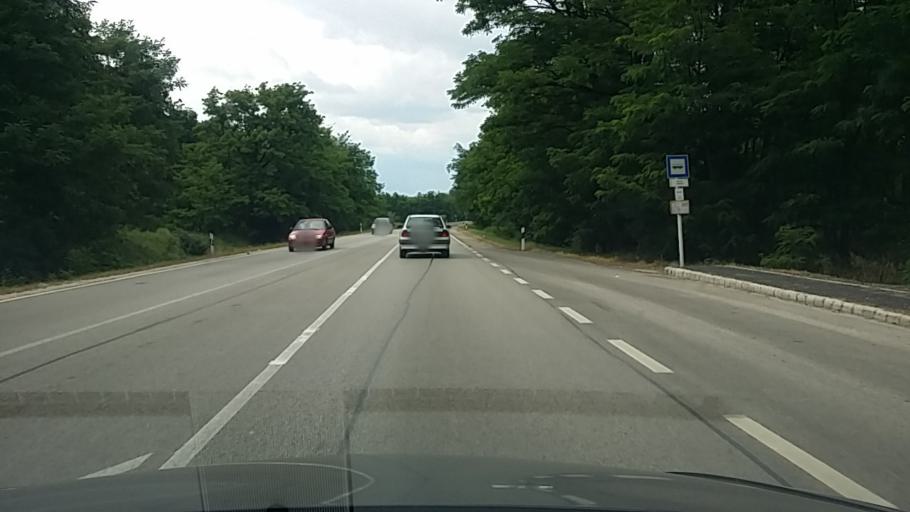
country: HU
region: Pest
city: Hernad
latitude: 47.1525
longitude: 19.3887
